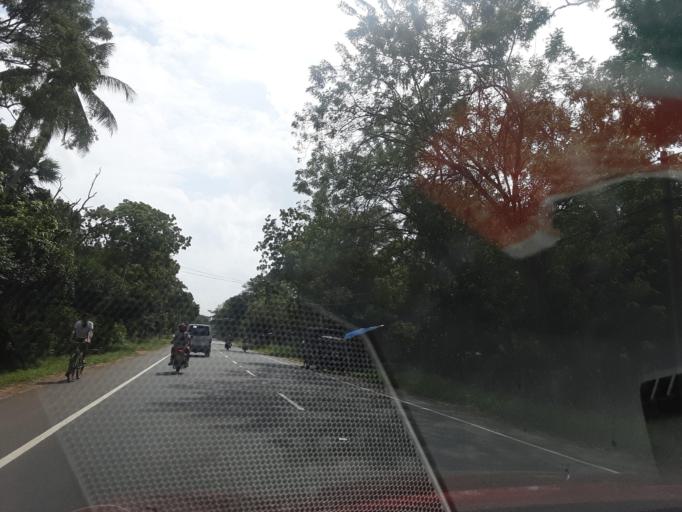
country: LK
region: North Central
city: Anuradhapura
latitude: 8.4969
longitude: 80.5121
